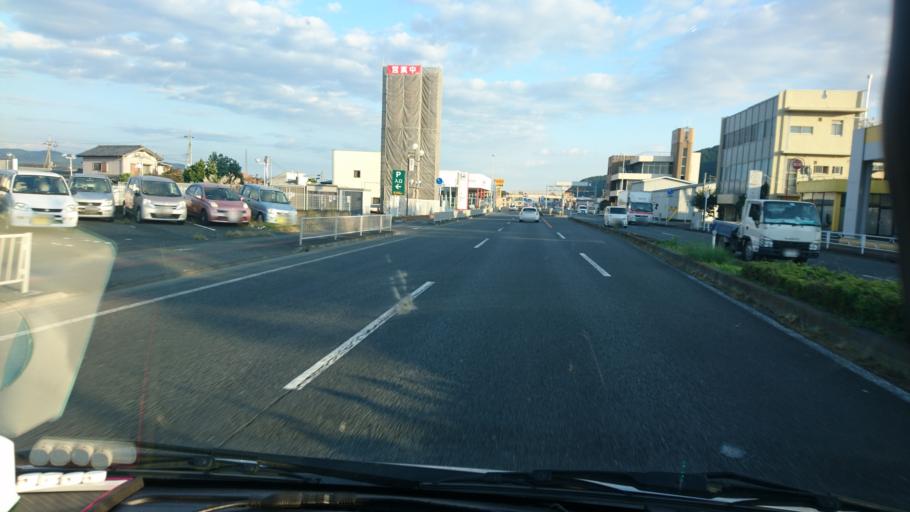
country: JP
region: Gunma
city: Kiryu
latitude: 36.3784
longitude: 139.3448
